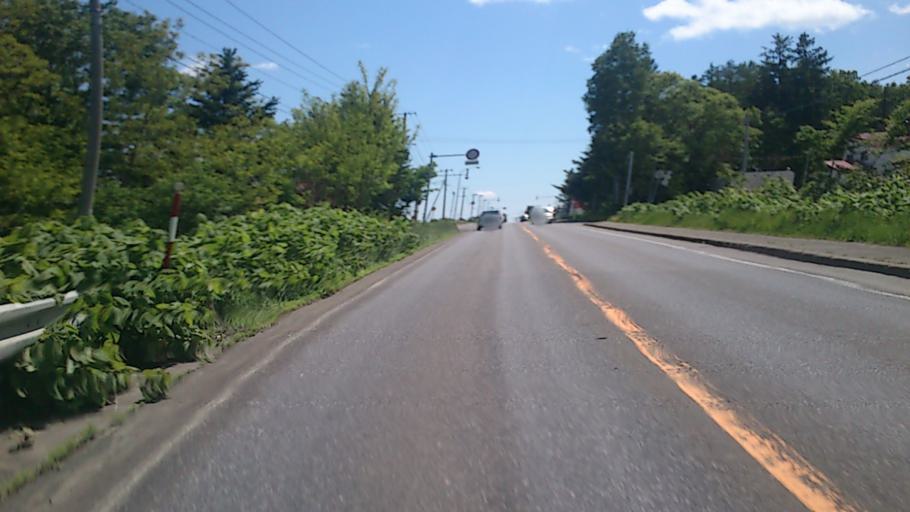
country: JP
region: Hokkaido
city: Nayoro
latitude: 44.2519
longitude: 142.3948
